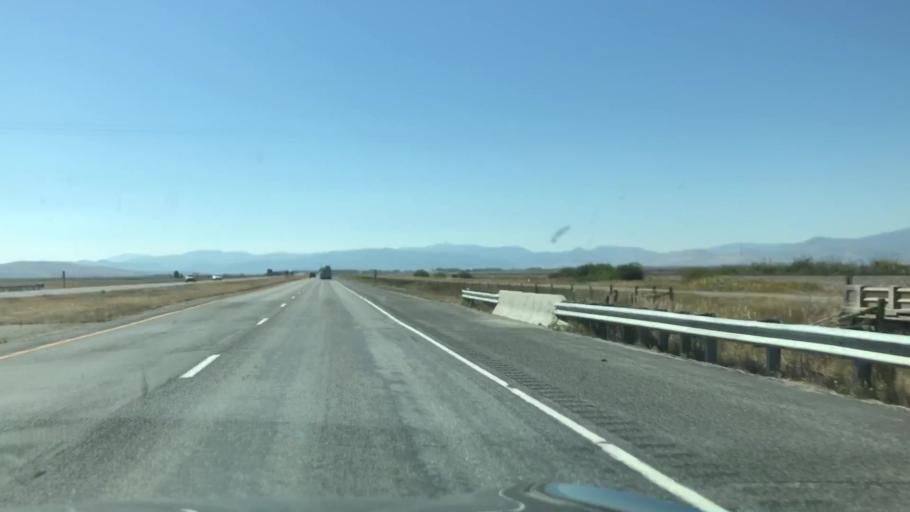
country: US
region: Montana
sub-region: Deer Lodge County
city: Warm Springs
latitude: 46.2187
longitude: -112.7732
